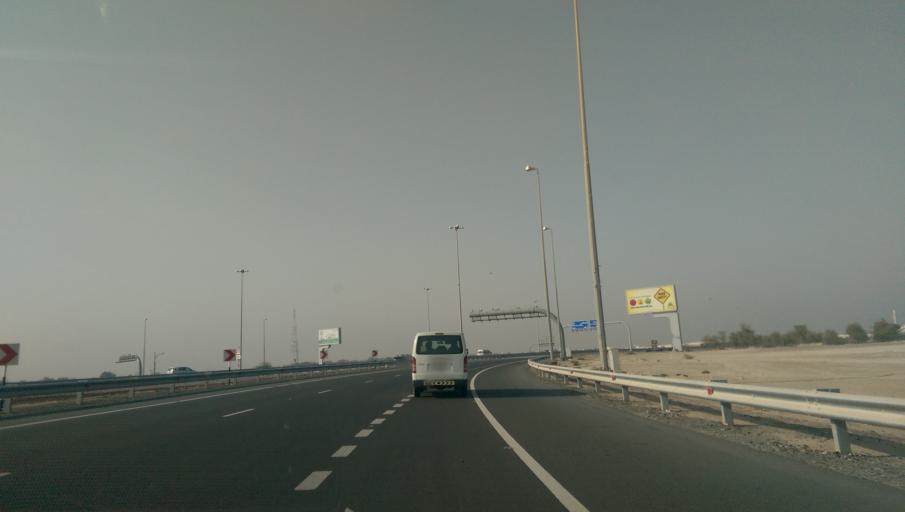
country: AE
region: Abu Dhabi
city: Abu Dhabi
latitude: 24.6927
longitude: 54.7767
